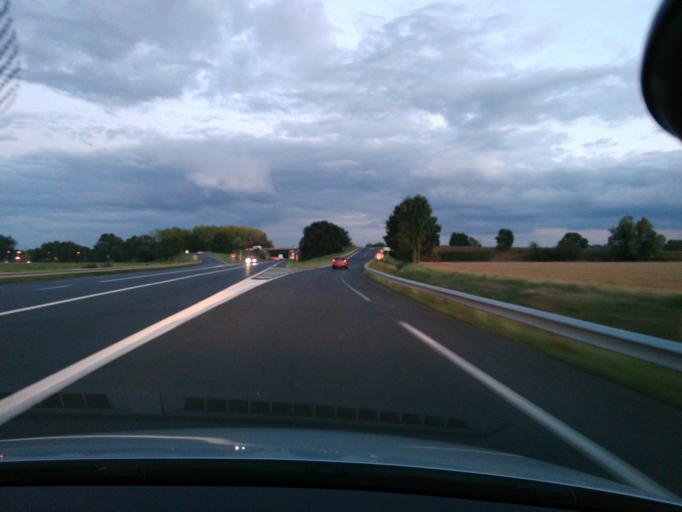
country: FR
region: Ile-de-France
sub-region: Departement de Seine-et-Marne
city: Villiers-sur-Morin
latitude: 48.8572
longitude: 2.8526
